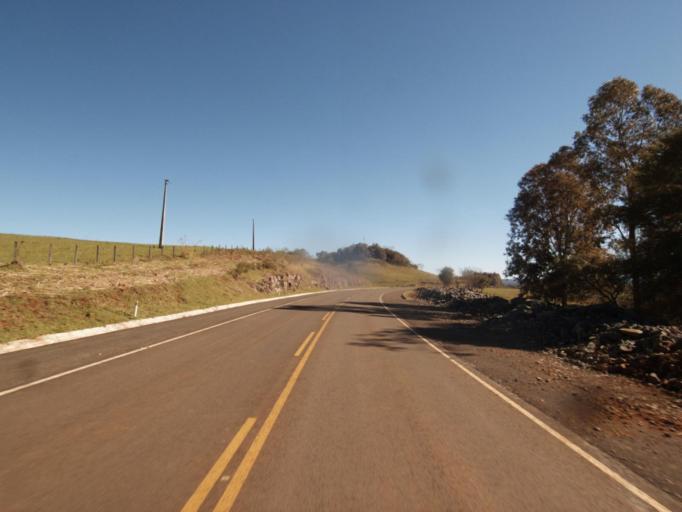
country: AR
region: Misiones
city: Bernardo de Irigoyen
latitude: -26.6146
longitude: -53.7057
